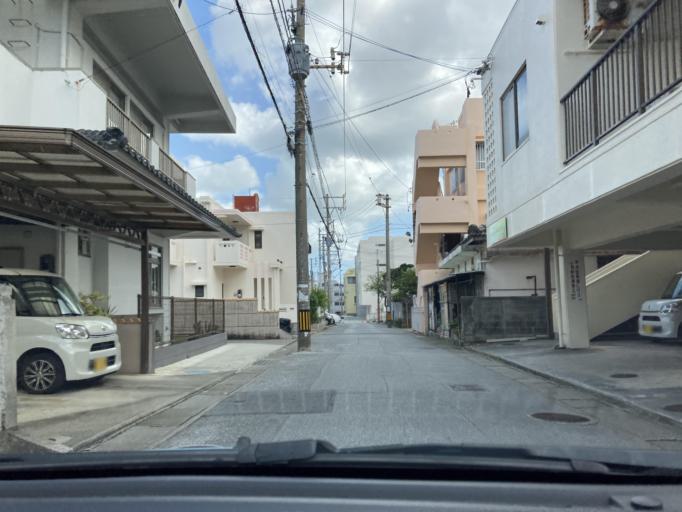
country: JP
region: Okinawa
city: Tomigusuku
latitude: 26.1986
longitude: 127.6741
